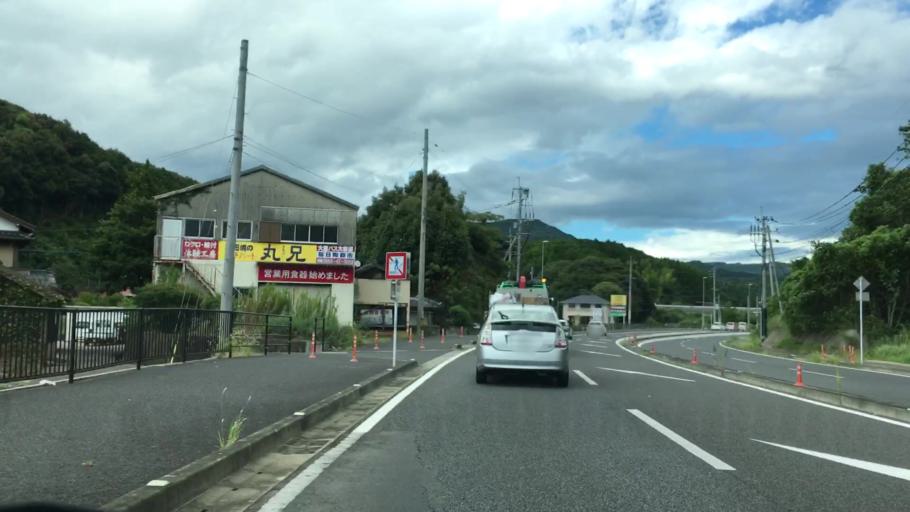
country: JP
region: Saga Prefecture
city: Imaricho-ko
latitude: 33.2786
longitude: 129.8950
